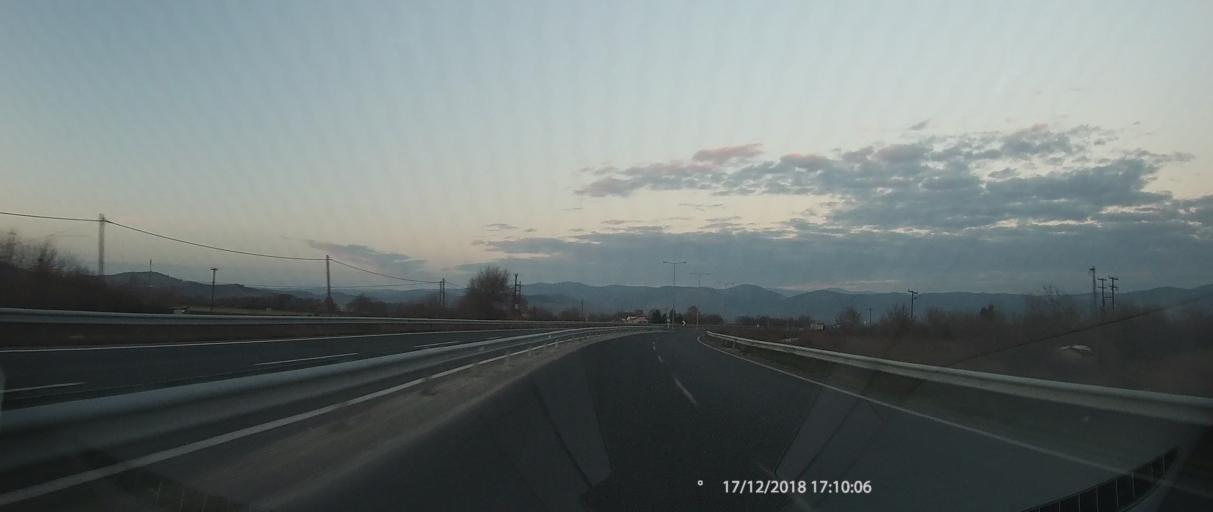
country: GR
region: Thessaly
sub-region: Trikala
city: Trikala
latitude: 39.5622
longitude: 21.8018
